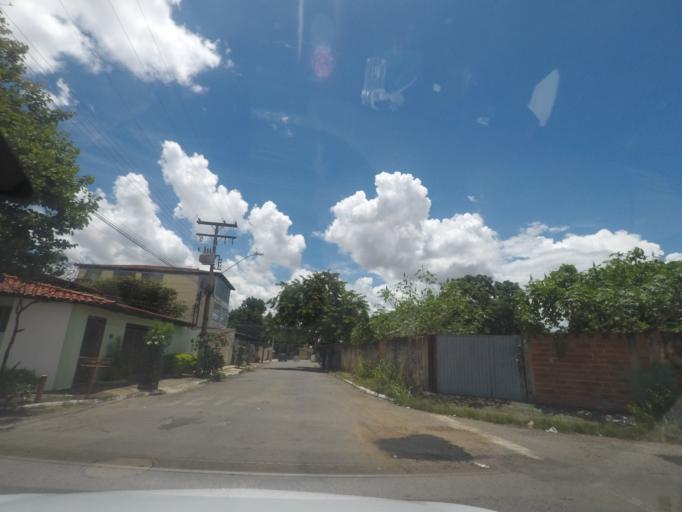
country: BR
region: Goias
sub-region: Goiania
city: Goiania
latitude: -16.6647
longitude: -49.2871
